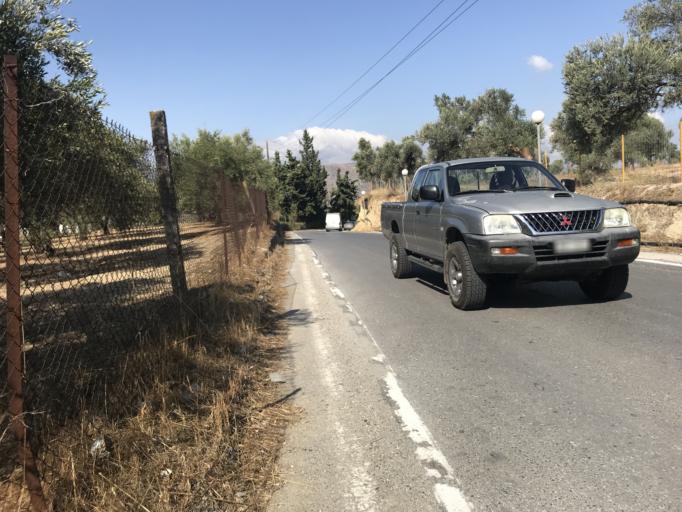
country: GR
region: Crete
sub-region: Nomos Irakleiou
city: Gazi
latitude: 35.3040
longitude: 25.0768
